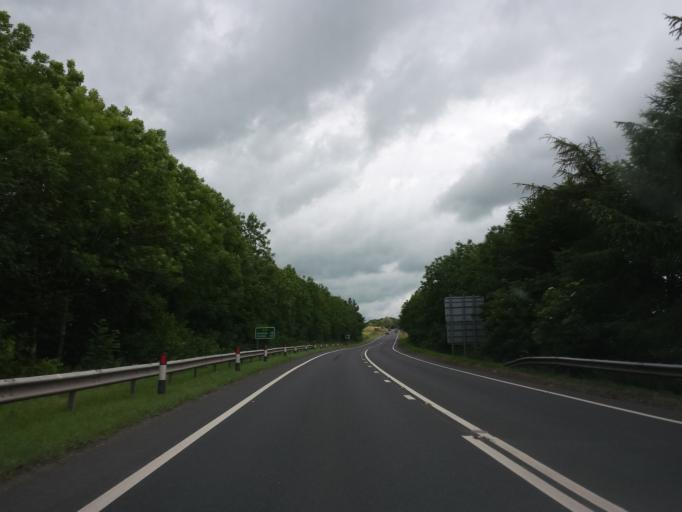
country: GB
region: Scotland
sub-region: Dumfries and Galloway
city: Castle Douglas
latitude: 54.9474
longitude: -3.9406
